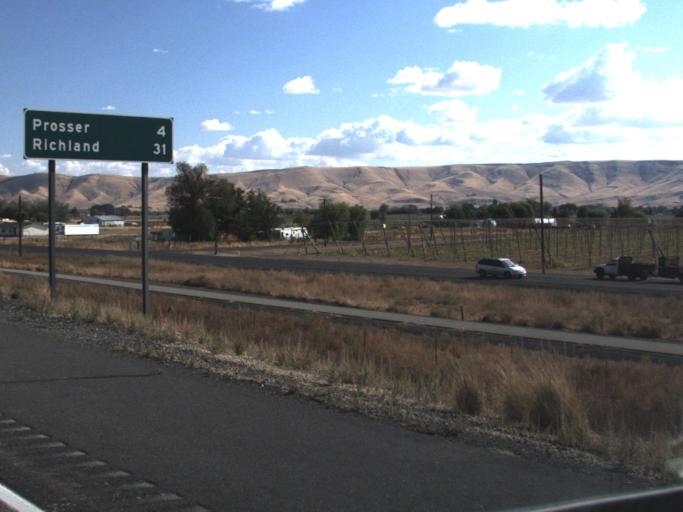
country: US
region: Washington
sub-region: Yakima County
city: Grandview
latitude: 46.2443
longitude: -119.8429
